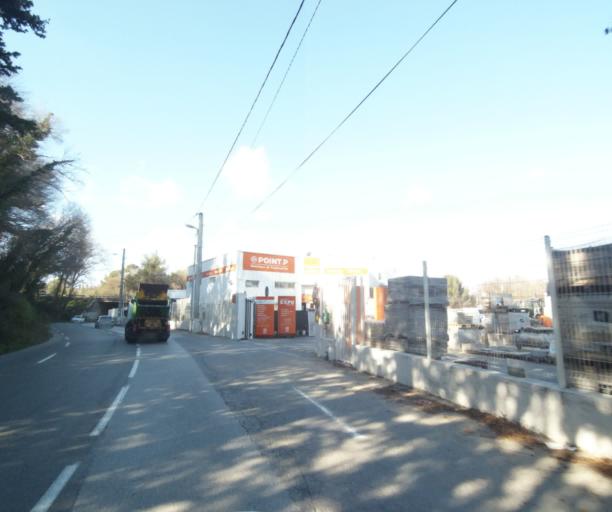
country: FR
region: Provence-Alpes-Cote d'Azur
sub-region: Departement des Alpes-Maritimes
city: Biot
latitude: 43.6109
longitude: 7.1097
